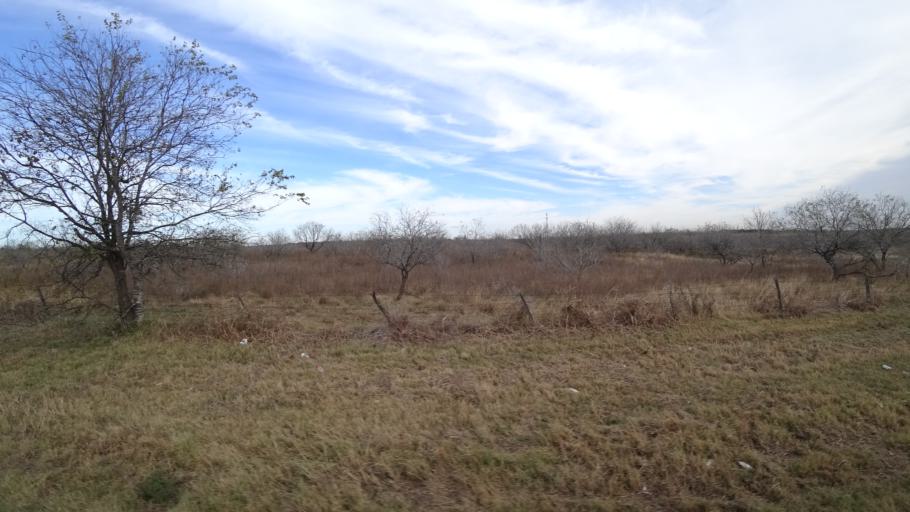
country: US
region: Texas
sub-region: Travis County
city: Onion Creek
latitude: 30.1302
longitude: -97.7127
